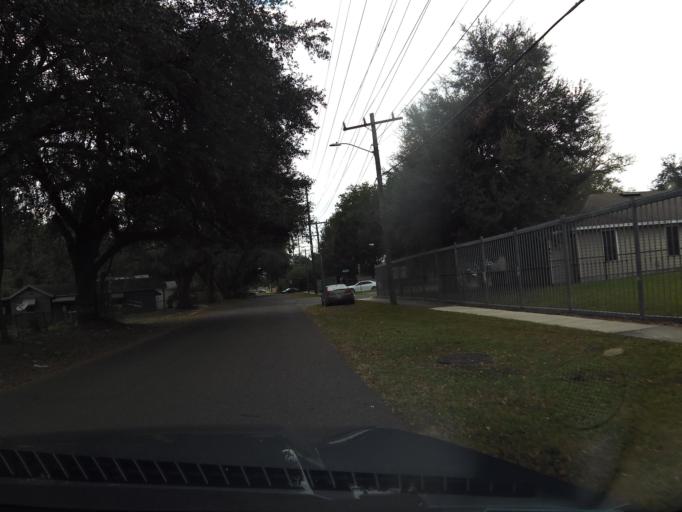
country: US
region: Florida
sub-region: Duval County
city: Jacksonville
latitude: 30.3620
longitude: -81.6661
